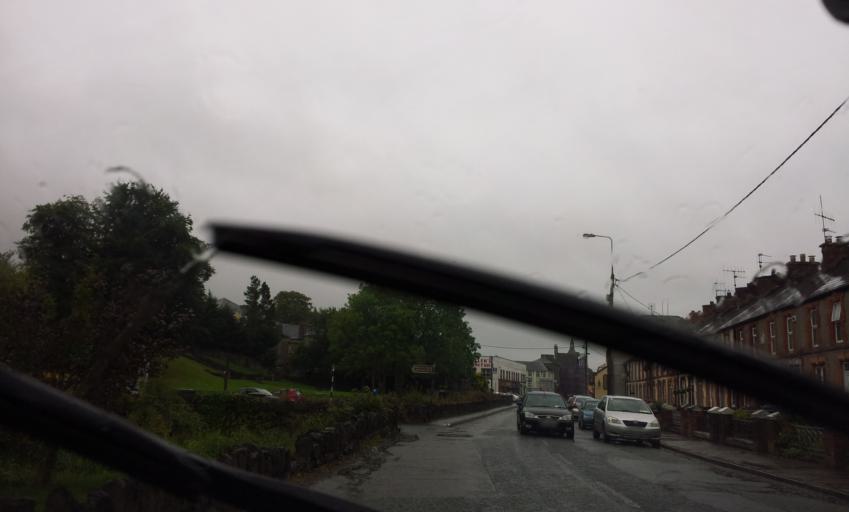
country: IE
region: Munster
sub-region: County Cork
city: Mallow
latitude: 52.1375
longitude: -8.6394
